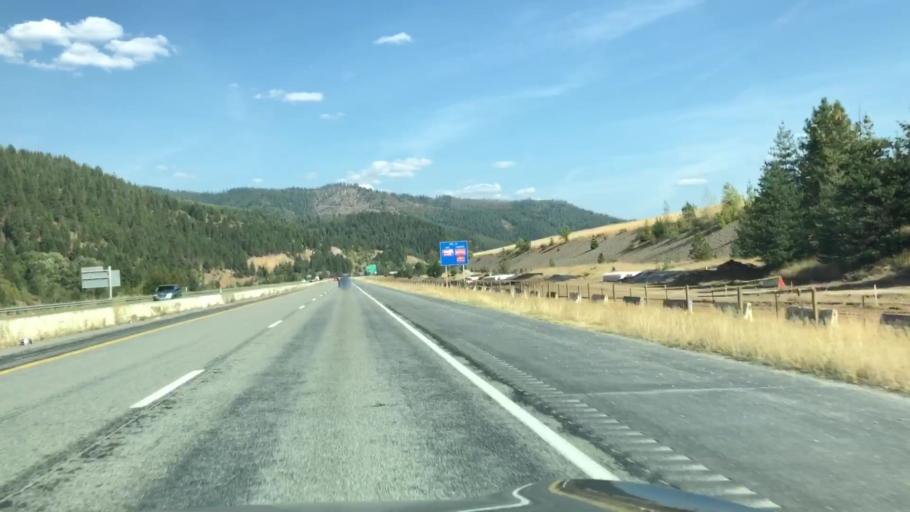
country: US
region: Idaho
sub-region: Shoshone County
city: Kellogg
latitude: 47.5481
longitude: -116.1520
